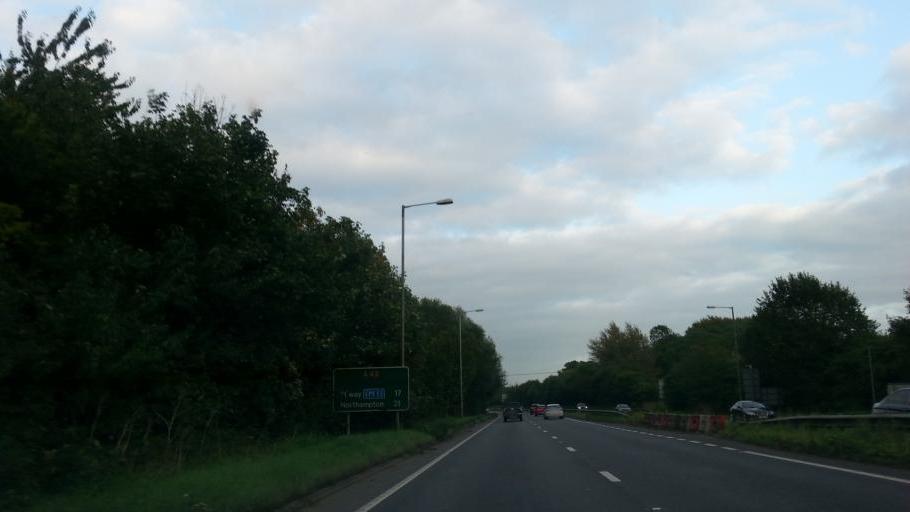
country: GB
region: England
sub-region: Northamptonshire
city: Brackley
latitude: 52.0213
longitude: -1.1483
